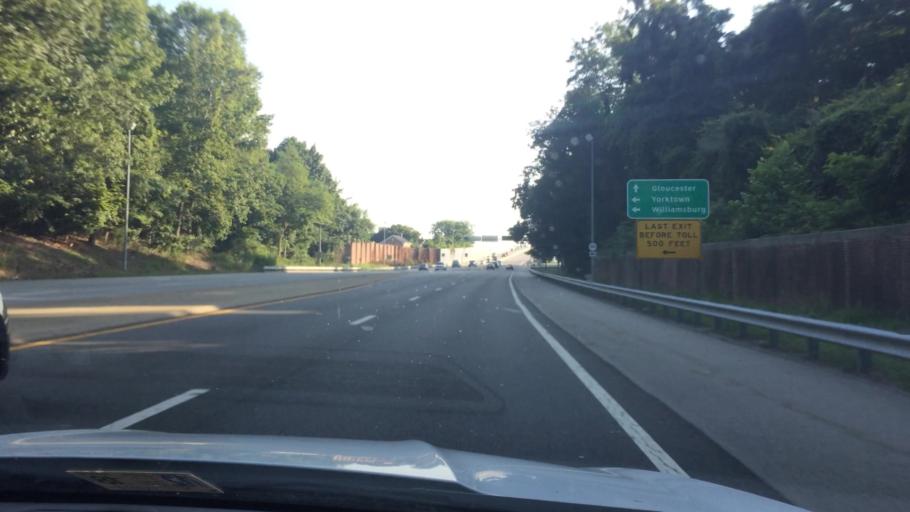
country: US
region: Virginia
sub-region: York County
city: Yorktown
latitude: 37.2358
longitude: -76.5118
